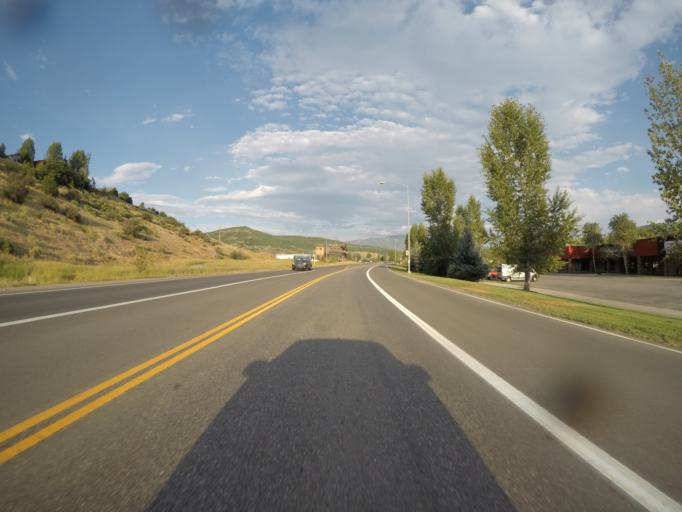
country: US
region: Colorado
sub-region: Routt County
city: Steamboat Springs
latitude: 40.5040
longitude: -106.8680
